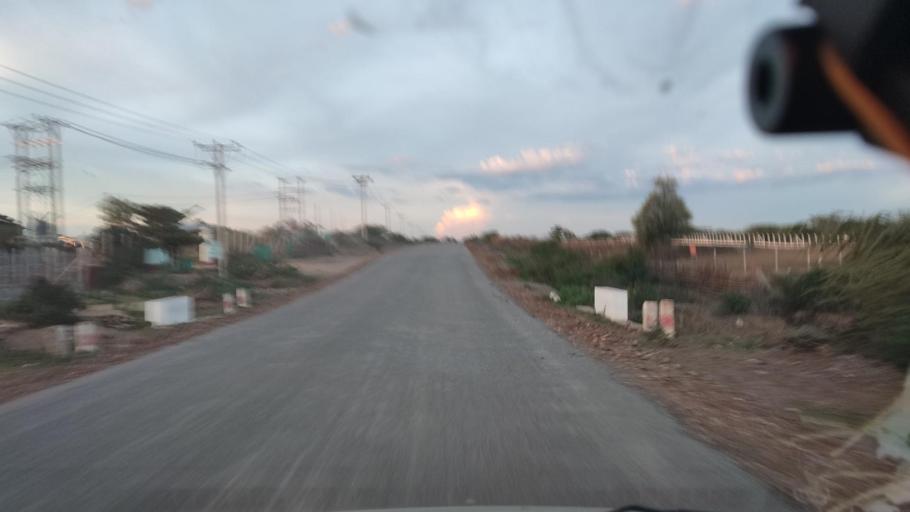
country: MM
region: Magway
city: Magway
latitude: 20.1855
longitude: 94.9464
